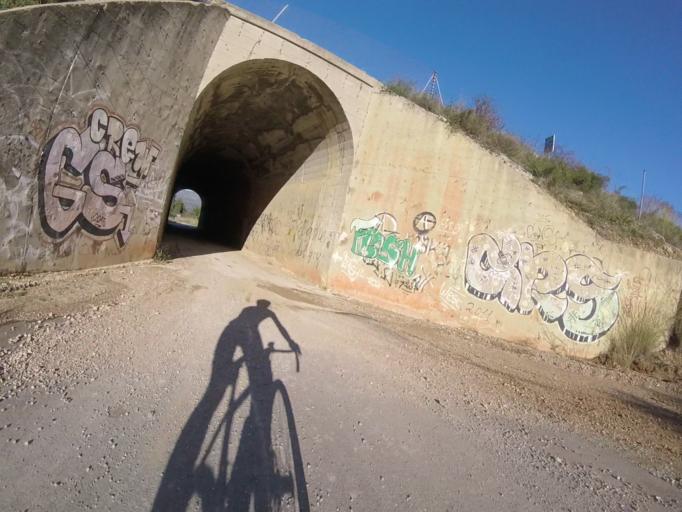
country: ES
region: Valencia
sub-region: Provincia de Castello
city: Santa Magdalena de Pulpis
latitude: 40.3542
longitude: 0.3117
